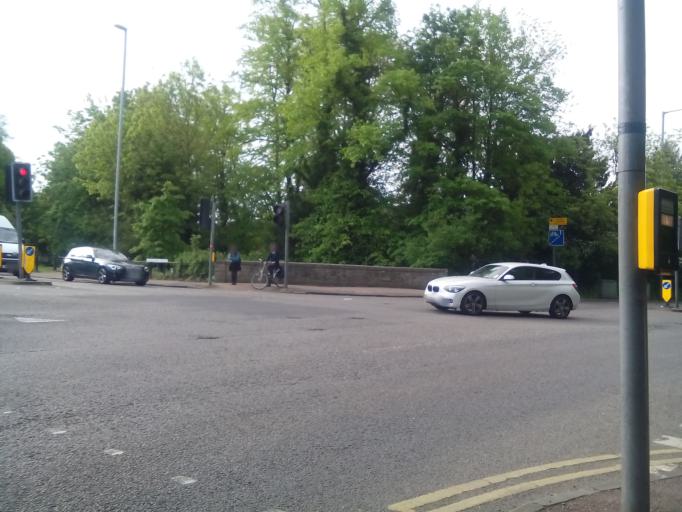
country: GB
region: England
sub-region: Cambridgeshire
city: Cambridge
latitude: 52.1918
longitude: 0.1238
